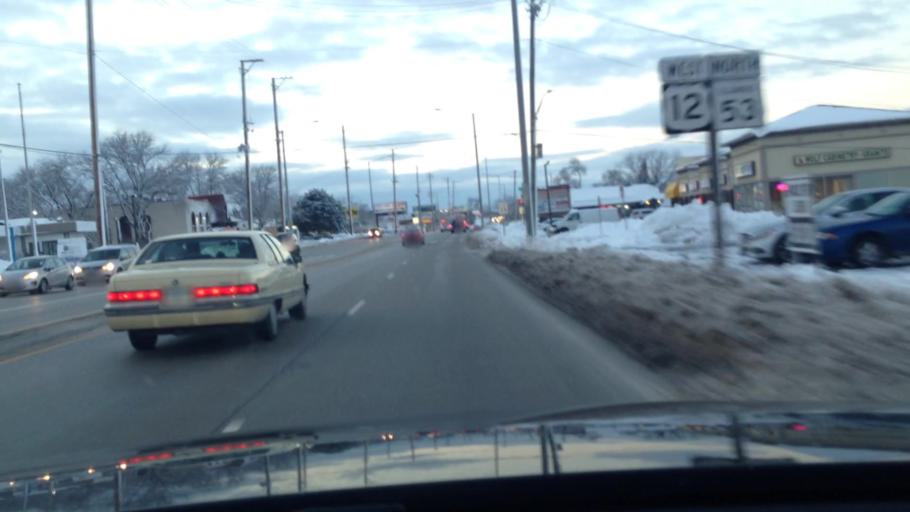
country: US
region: Illinois
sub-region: Cook County
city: Palatine
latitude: 42.1395
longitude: -88.0223
